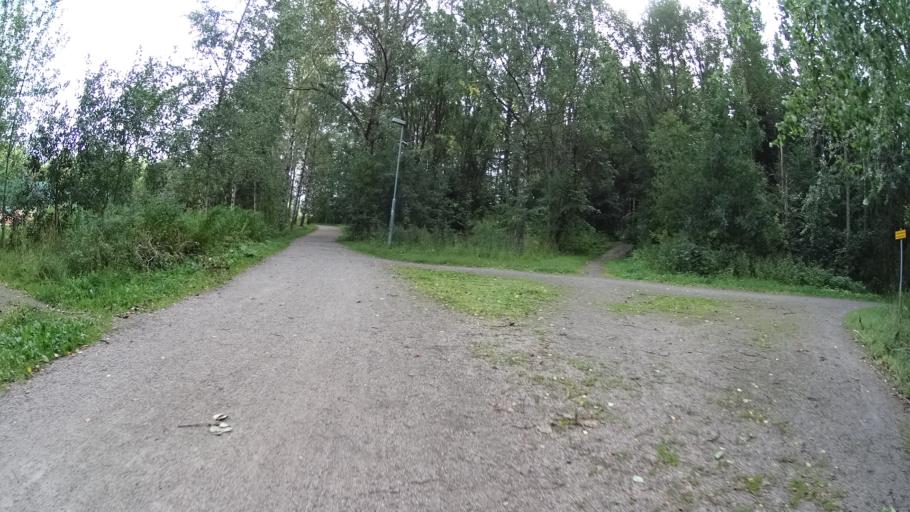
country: FI
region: Uusimaa
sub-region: Helsinki
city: Teekkarikylae
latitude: 60.2117
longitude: 24.8751
